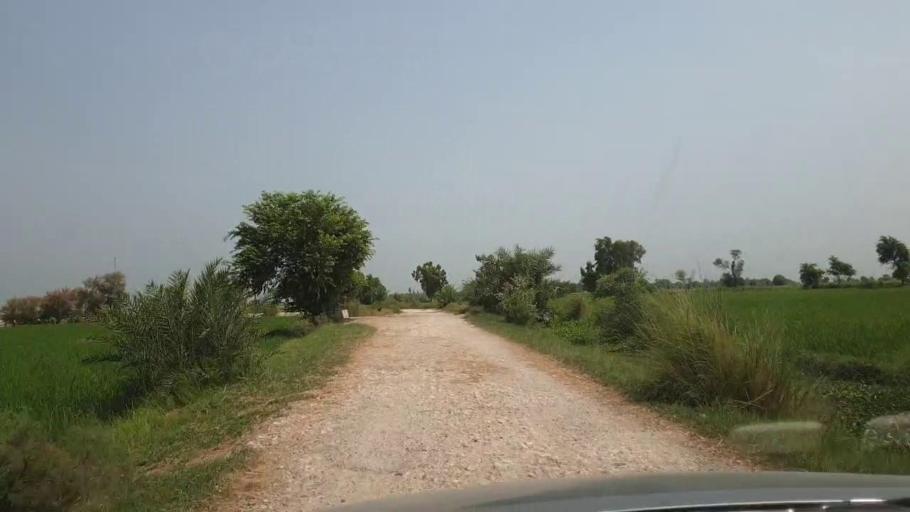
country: PK
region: Sindh
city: Madeji
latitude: 27.7968
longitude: 68.5321
